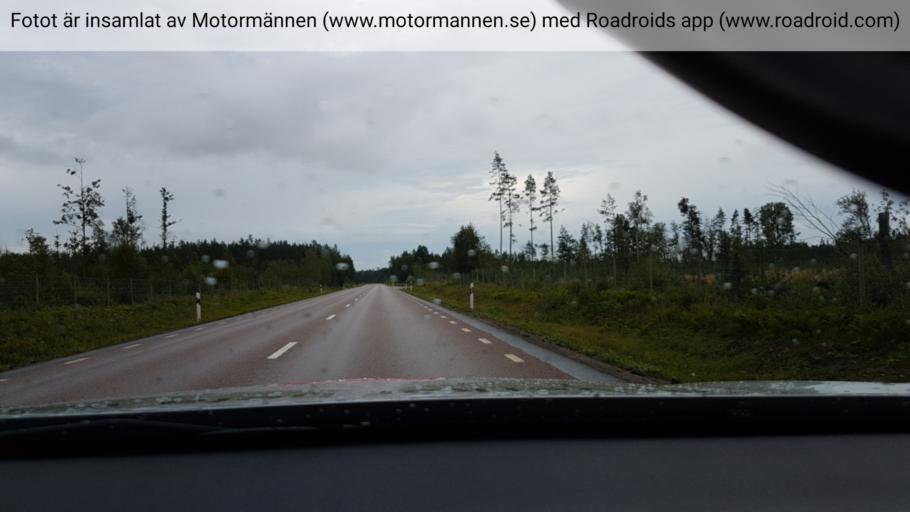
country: SE
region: Uppsala
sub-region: Tierps Kommun
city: Karlholmsbruk
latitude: 60.4347
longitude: 17.8000
